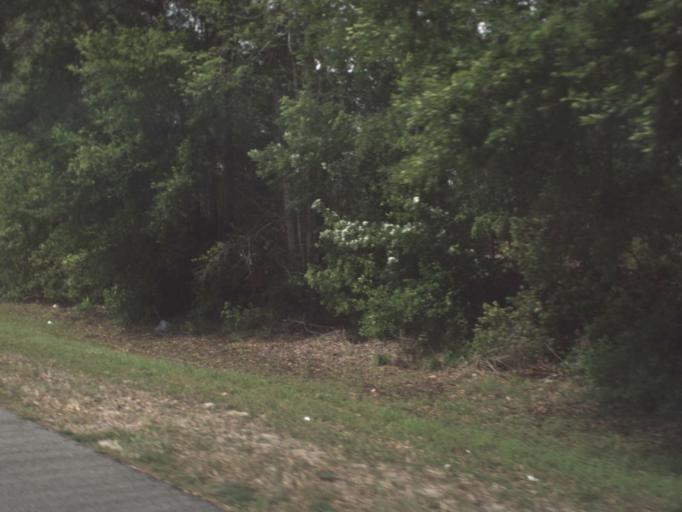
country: US
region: Florida
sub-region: Flagler County
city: Bunnell
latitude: 29.4758
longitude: -81.3320
